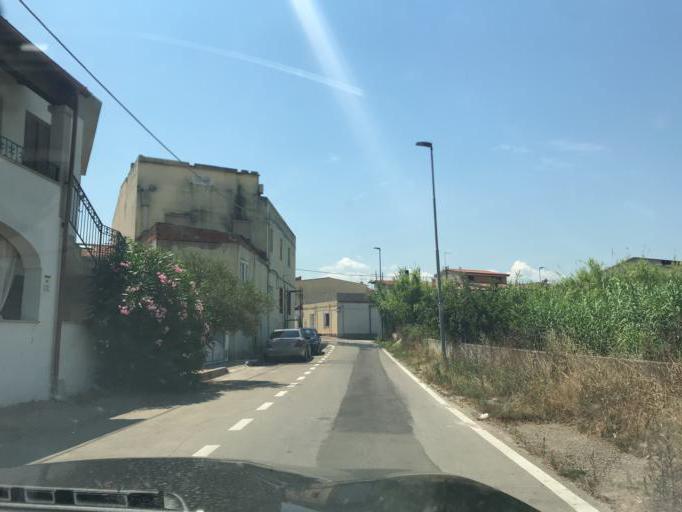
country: IT
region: Sardinia
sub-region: Provincia di Olbia-Tempio
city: Olbia
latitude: 40.9310
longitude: 9.5067
